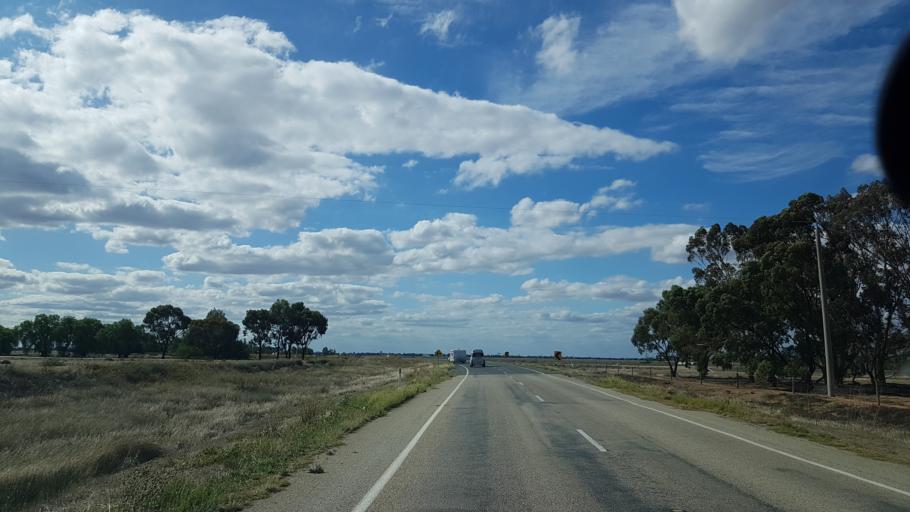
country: AU
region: Victoria
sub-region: Swan Hill
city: Swan Hill
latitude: -35.8018
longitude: 143.9554
